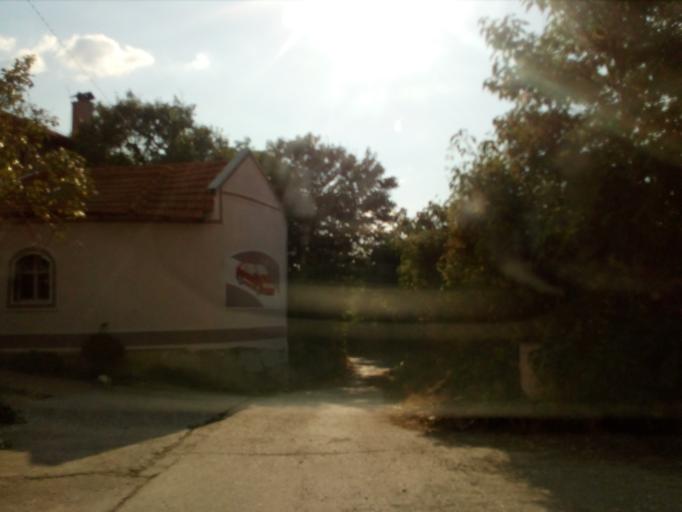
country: MK
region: Veles
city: Veles
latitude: 41.7447
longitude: 21.7926
